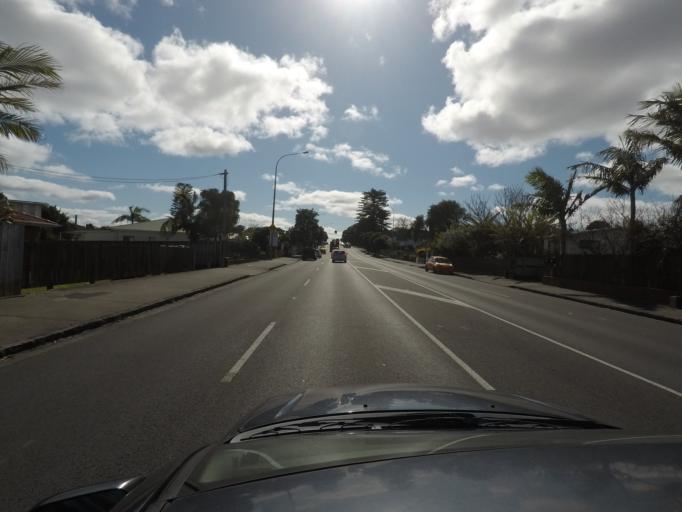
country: NZ
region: Auckland
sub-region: Auckland
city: Rosebank
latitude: -36.8904
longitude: 174.7091
